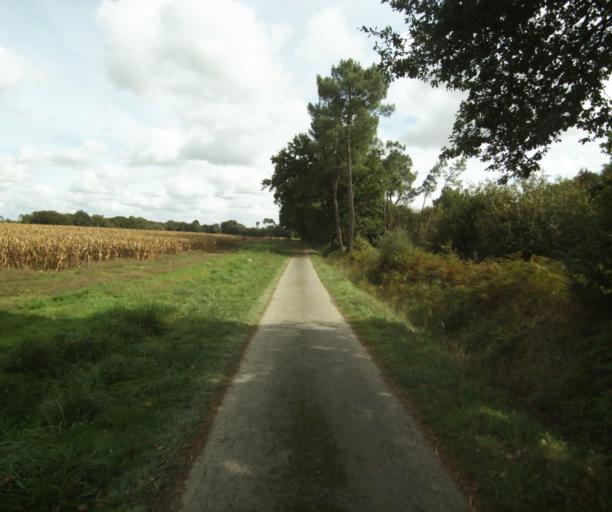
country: FR
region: Midi-Pyrenees
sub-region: Departement du Gers
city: Eauze
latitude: 43.8268
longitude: 0.1034
